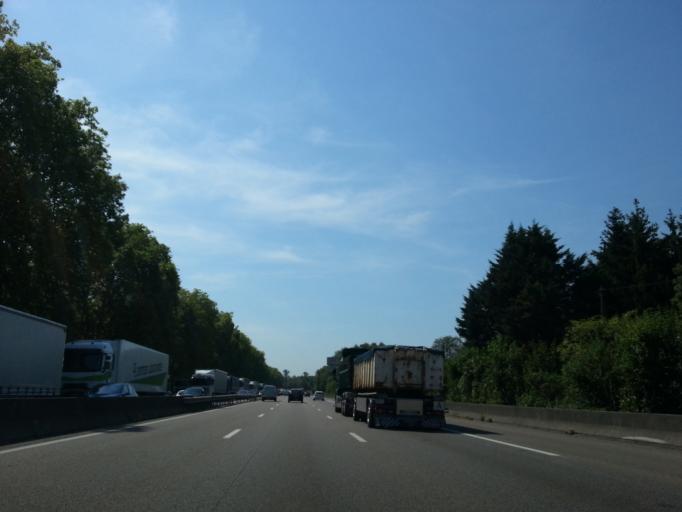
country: FR
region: Alsace
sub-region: Departement du Bas-Rhin
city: Ostwald
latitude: 48.5574
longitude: 7.7328
